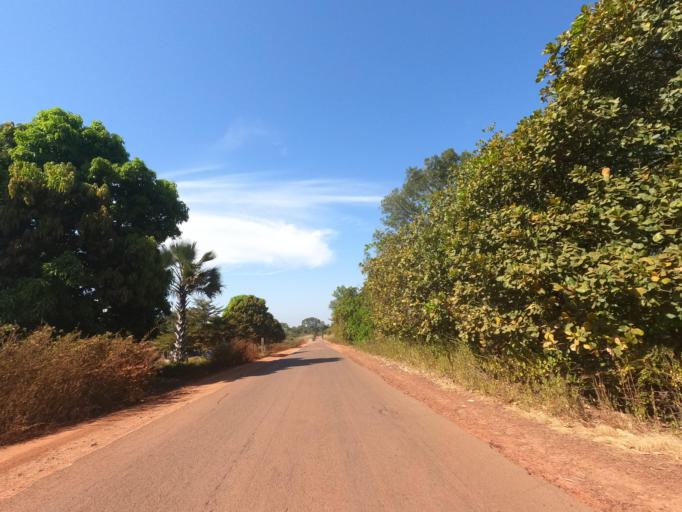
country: SN
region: Ziguinchor
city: Adeane
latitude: 12.3912
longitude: -15.8458
